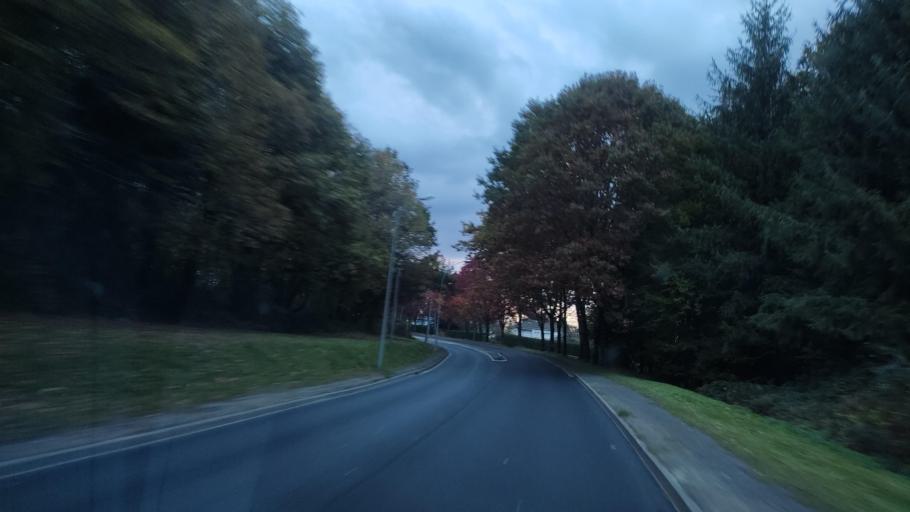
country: FR
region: Limousin
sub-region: Departement de la Haute-Vienne
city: Ambazac
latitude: 45.9449
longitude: 1.3911
